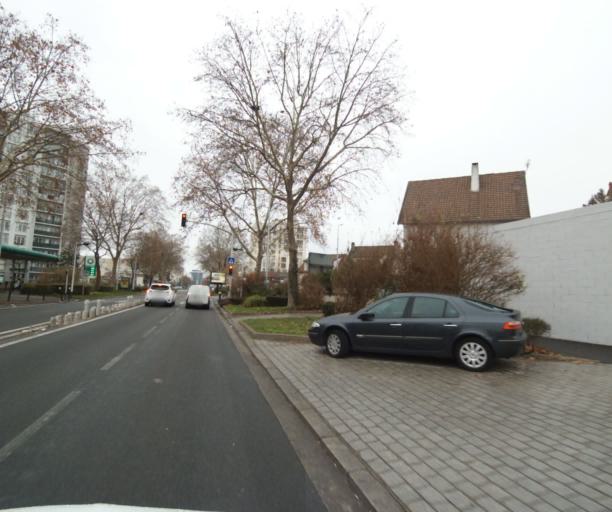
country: FR
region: Ile-de-France
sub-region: Departement des Hauts-de-Seine
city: Rueil-Malmaison
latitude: 48.8879
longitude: 2.1887
